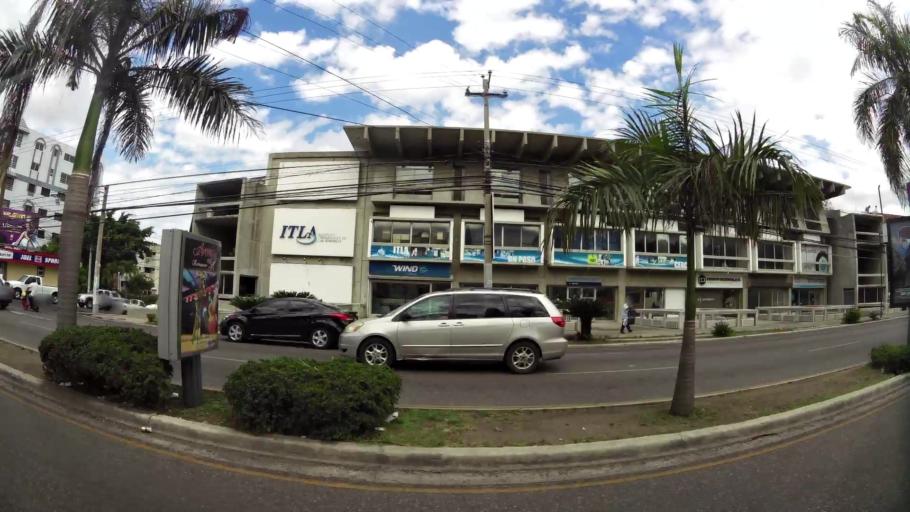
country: DO
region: Santiago
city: Santiago de los Caballeros
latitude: 19.4599
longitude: -70.6914
